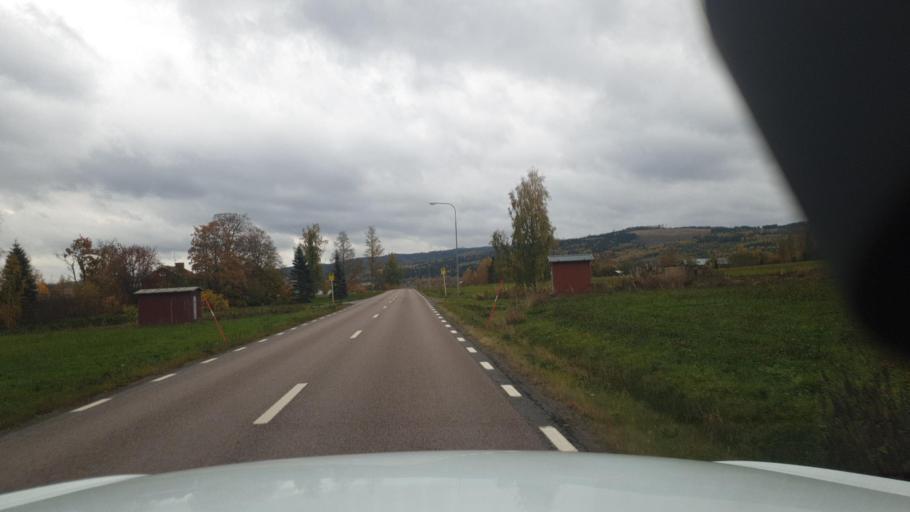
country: SE
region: Vaermland
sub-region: Sunne Kommun
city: Sunne
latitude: 59.8618
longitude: 12.9452
